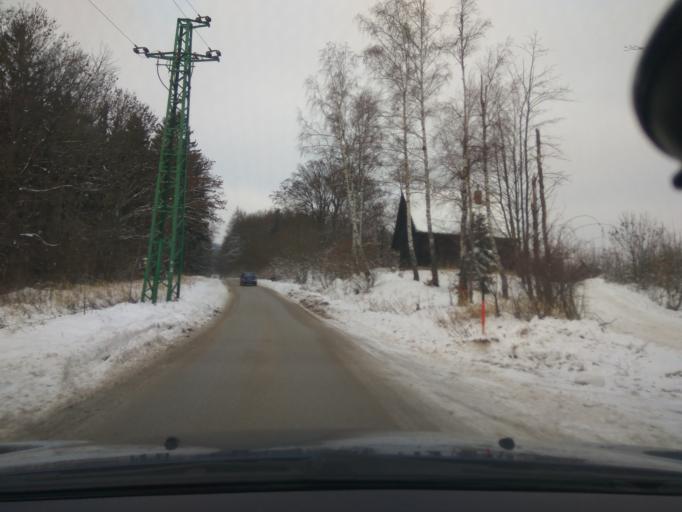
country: CZ
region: Zlin
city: Strani
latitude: 48.8464
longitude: 17.6920
